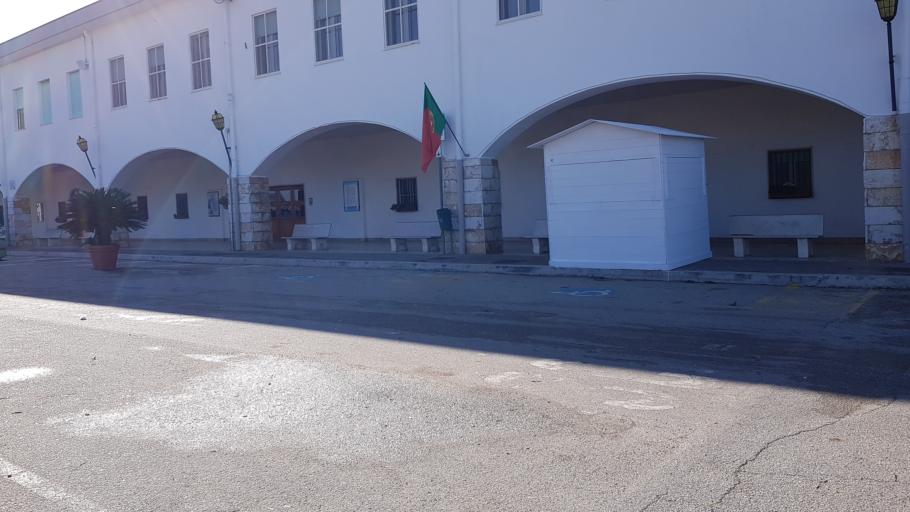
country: IT
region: Apulia
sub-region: Provincia di Foggia
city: Carapelle
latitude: 41.3820
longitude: 15.6403
